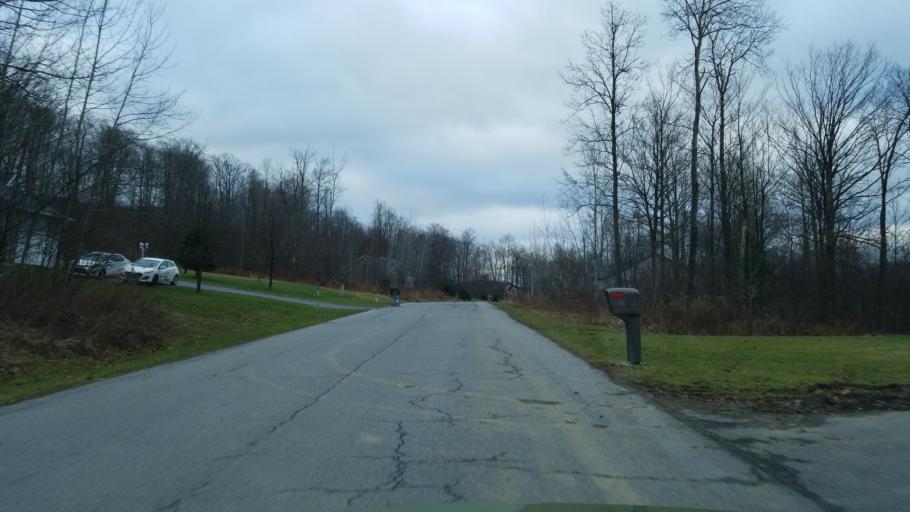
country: US
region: Pennsylvania
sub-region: Jefferson County
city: Falls Creek
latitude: 41.1380
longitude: -78.8101
